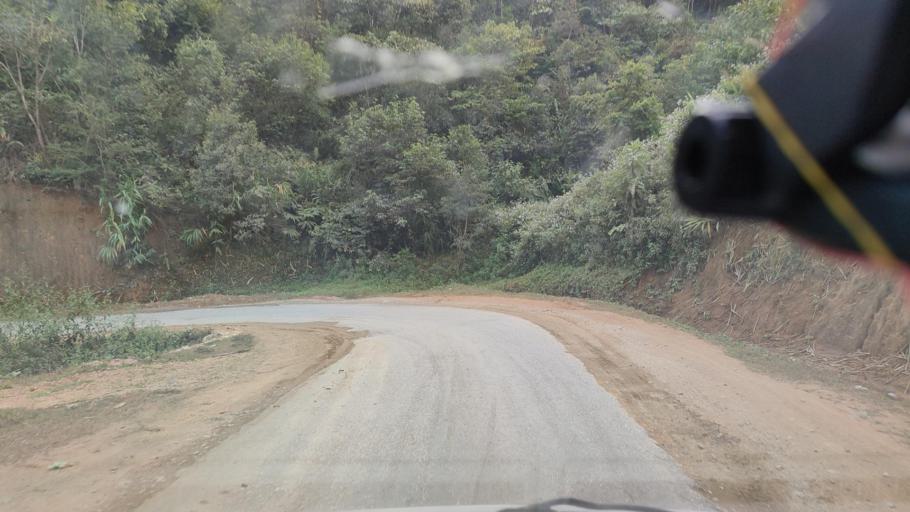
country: CN
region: Yunnan
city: Nayun
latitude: 21.7118
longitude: 99.4738
